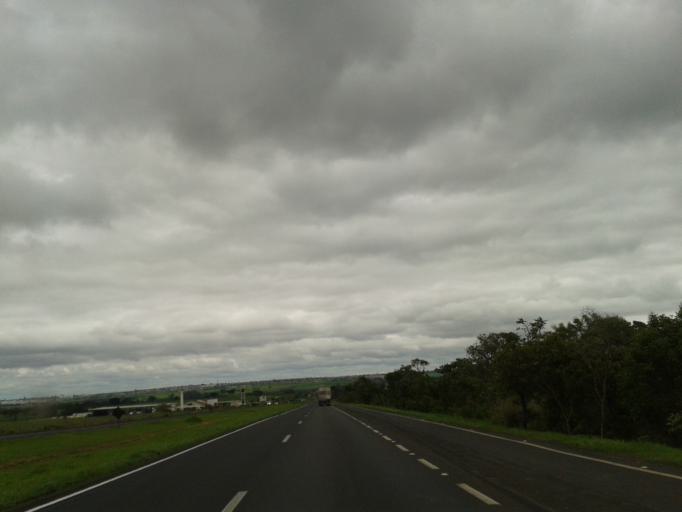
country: BR
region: Minas Gerais
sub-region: Uberlandia
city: Uberlandia
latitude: -19.0204
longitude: -48.2053
